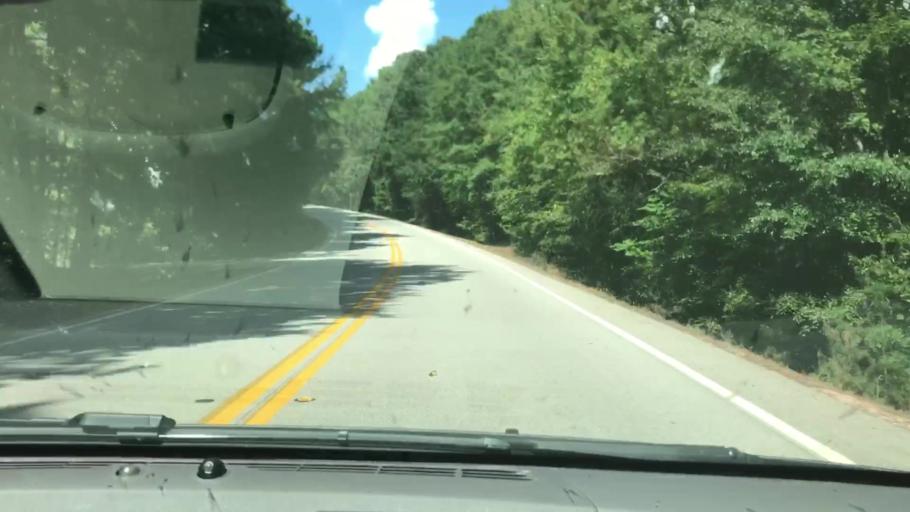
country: US
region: Georgia
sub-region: Troup County
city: La Grange
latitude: 33.1400
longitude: -85.0888
